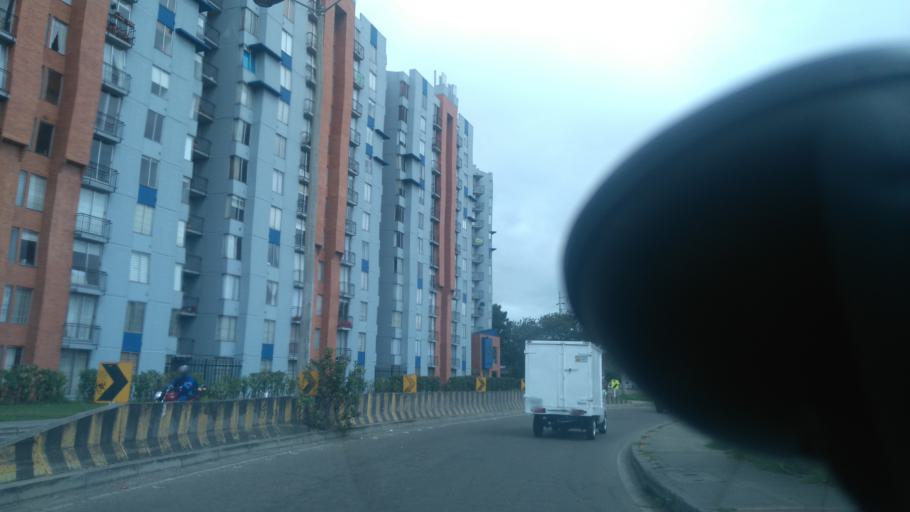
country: CO
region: Cundinamarca
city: Cota
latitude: 4.7511
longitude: -74.0481
